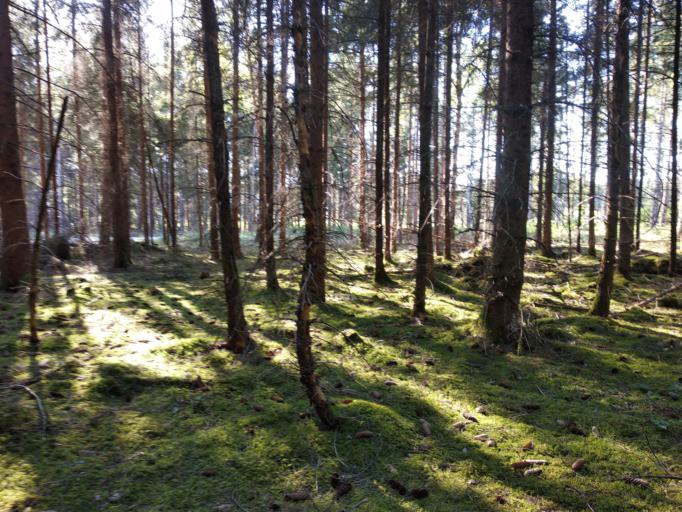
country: DE
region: Bavaria
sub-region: Upper Bavaria
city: Grasbrunn
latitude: 48.0924
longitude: 11.7483
